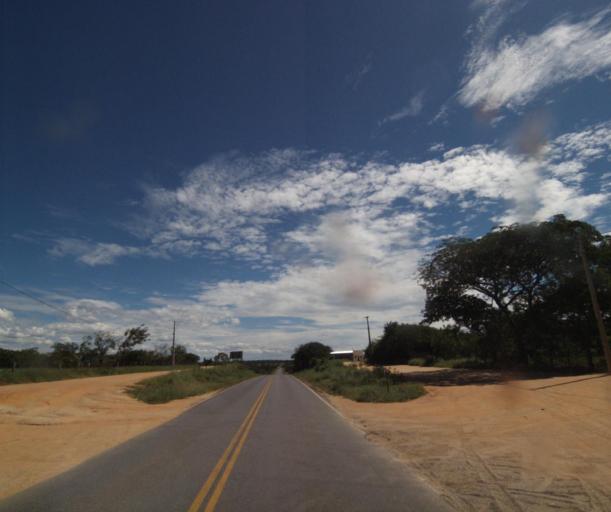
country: BR
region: Bahia
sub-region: Guanambi
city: Guanambi
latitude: -14.5513
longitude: -42.7009
